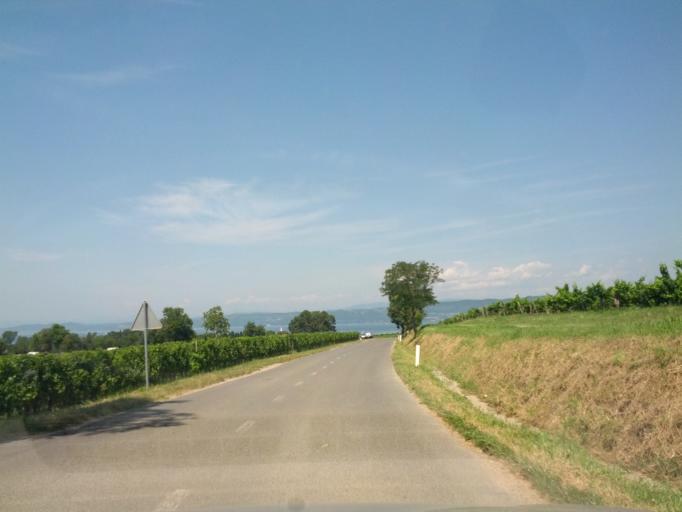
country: SI
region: Koper-Capodistria
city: Ankaran
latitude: 45.5859
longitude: 13.7135
